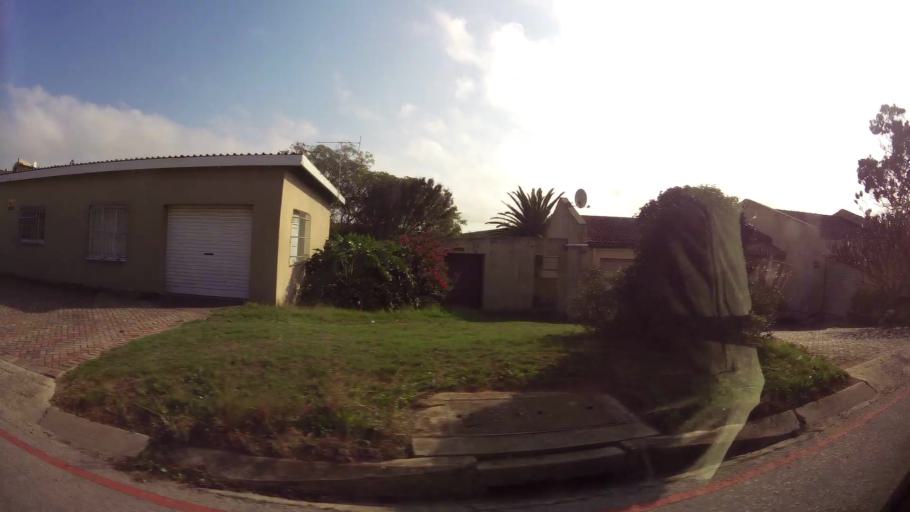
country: ZA
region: Eastern Cape
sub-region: Nelson Mandela Bay Metropolitan Municipality
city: Port Elizabeth
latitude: -33.9295
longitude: 25.5480
